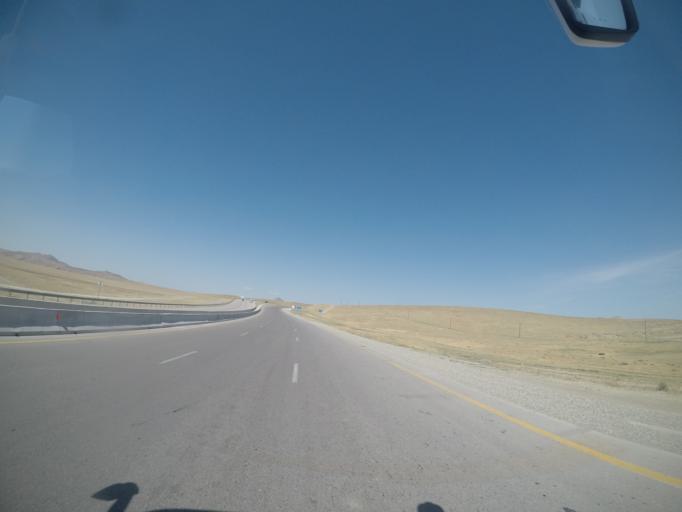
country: AZ
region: Sumqayit
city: Haci Zeynalabdin
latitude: 40.4760
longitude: 49.4606
